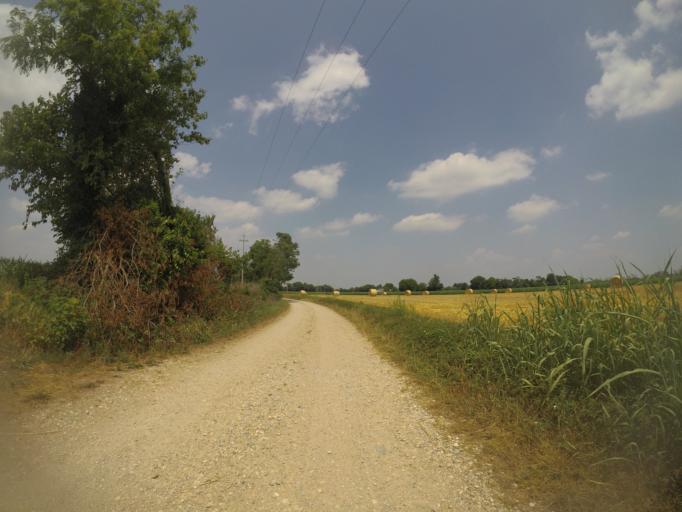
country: IT
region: Friuli Venezia Giulia
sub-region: Provincia di Udine
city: Bertiolo
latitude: 45.9651
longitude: 13.0677
